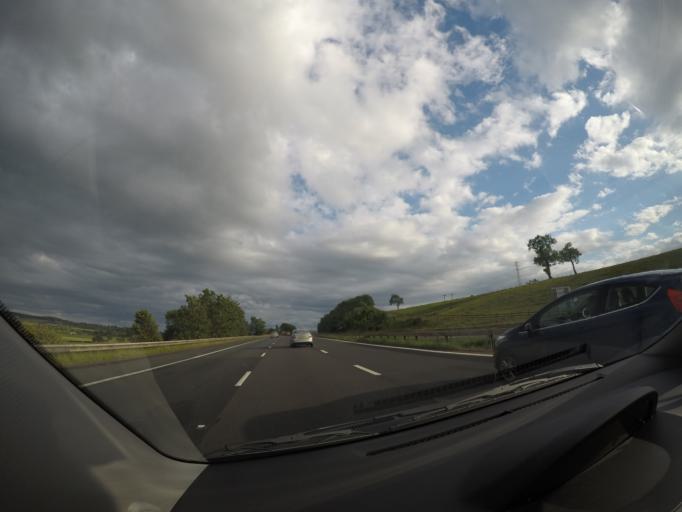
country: GB
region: England
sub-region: Cumbria
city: Penrith
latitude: 54.7021
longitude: -2.7914
